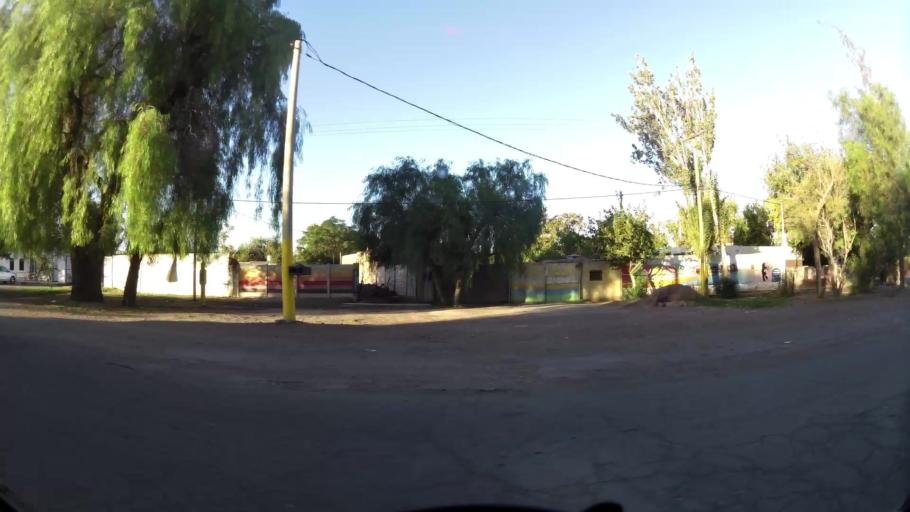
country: AR
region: San Juan
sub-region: Departamento de Santa Lucia
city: Santa Lucia
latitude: -31.5433
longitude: -68.4920
